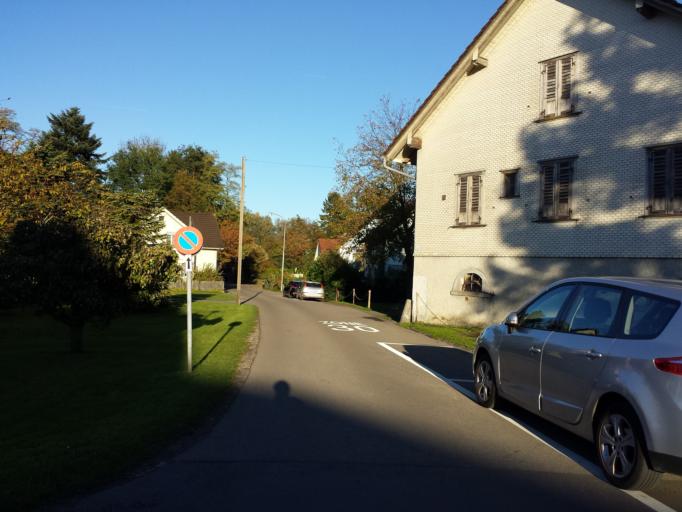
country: CH
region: Thurgau
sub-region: Arbon District
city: Egnach
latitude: 47.5467
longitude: 9.3824
